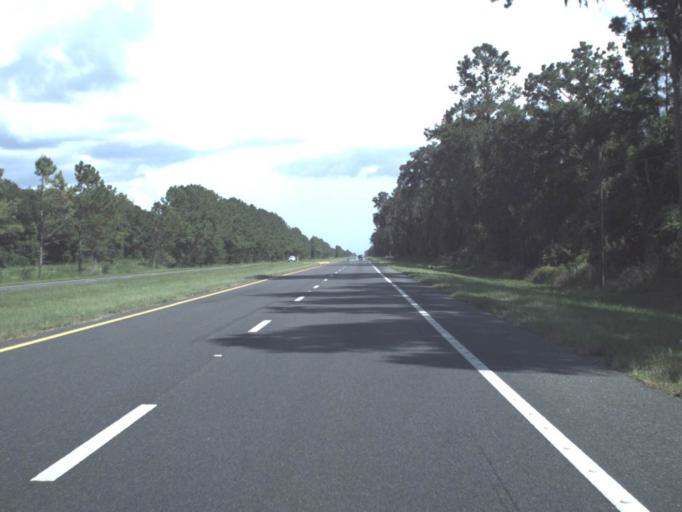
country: US
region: Florida
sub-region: Levy County
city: Chiefland
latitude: 29.4463
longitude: -82.8414
